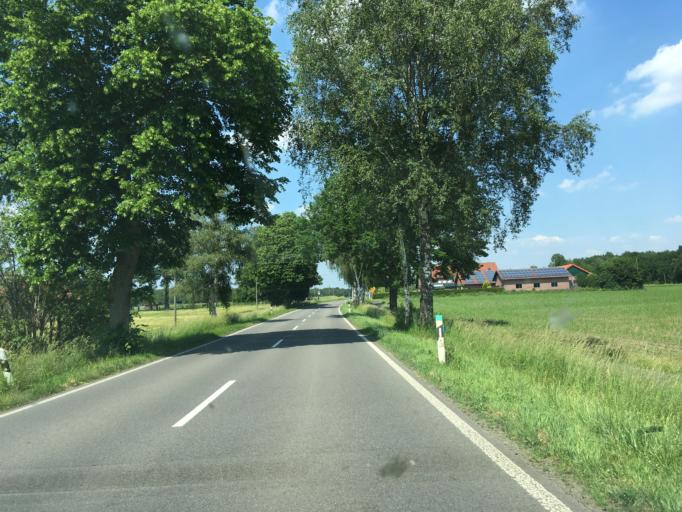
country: DE
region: North Rhine-Westphalia
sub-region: Regierungsbezirk Munster
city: Borken
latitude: 51.8488
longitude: 6.7814
